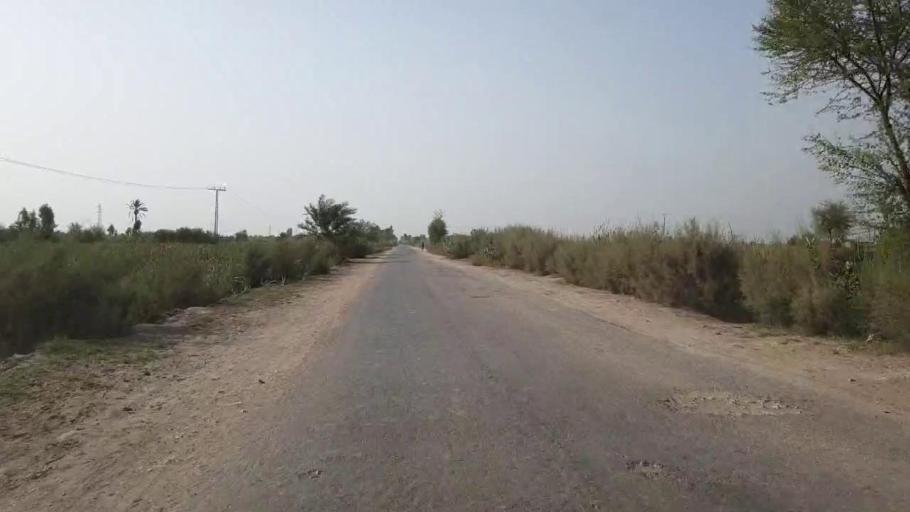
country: PK
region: Sindh
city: Khadro
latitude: 26.3287
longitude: 68.9305
